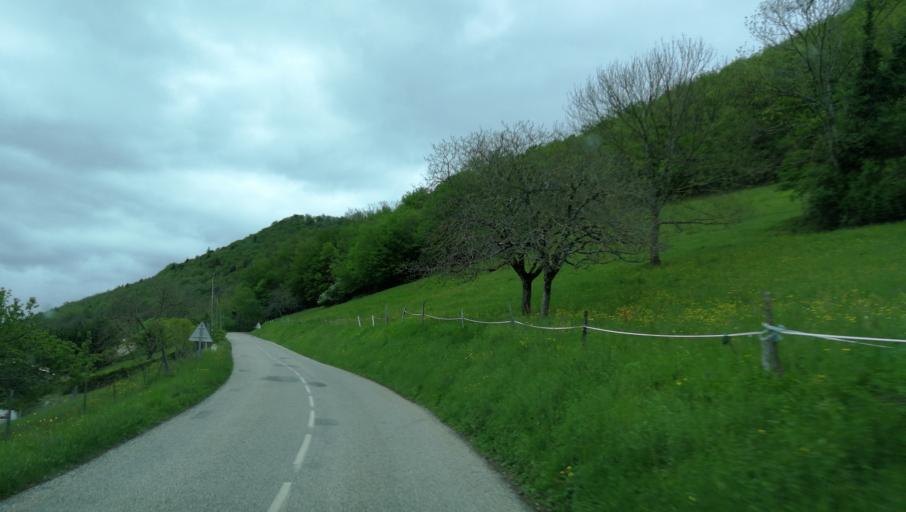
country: FR
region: Rhone-Alpes
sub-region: Departement de la Drome
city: Saint-Jean-en-Royans
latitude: 45.0061
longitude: 5.2962
